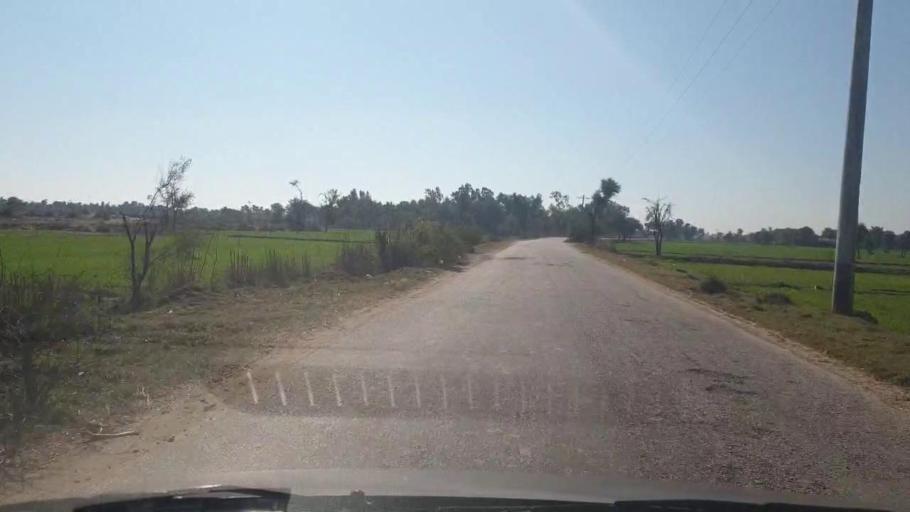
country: PK
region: Sindh
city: Bozdar
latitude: 27.0890
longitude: 68.6239
